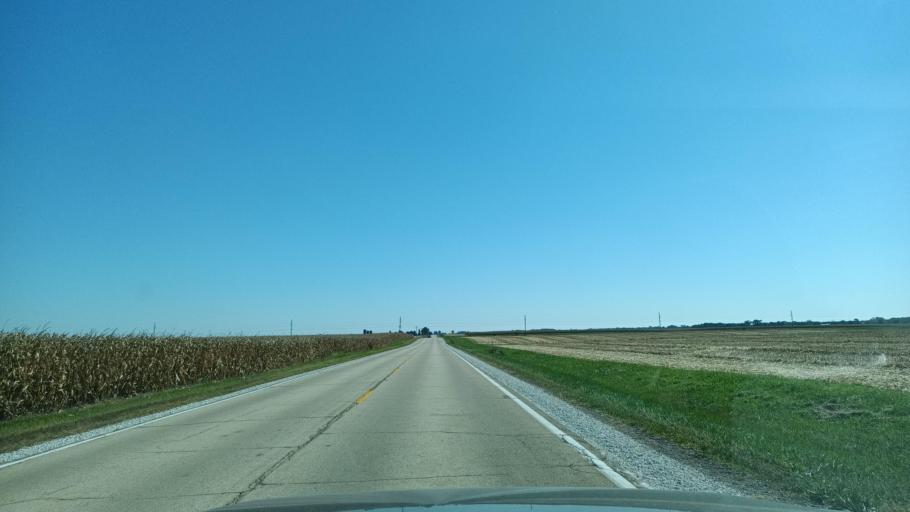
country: US
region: Illinois
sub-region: Peoria County
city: Elmwood
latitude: 40.9022
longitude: -89.9717
